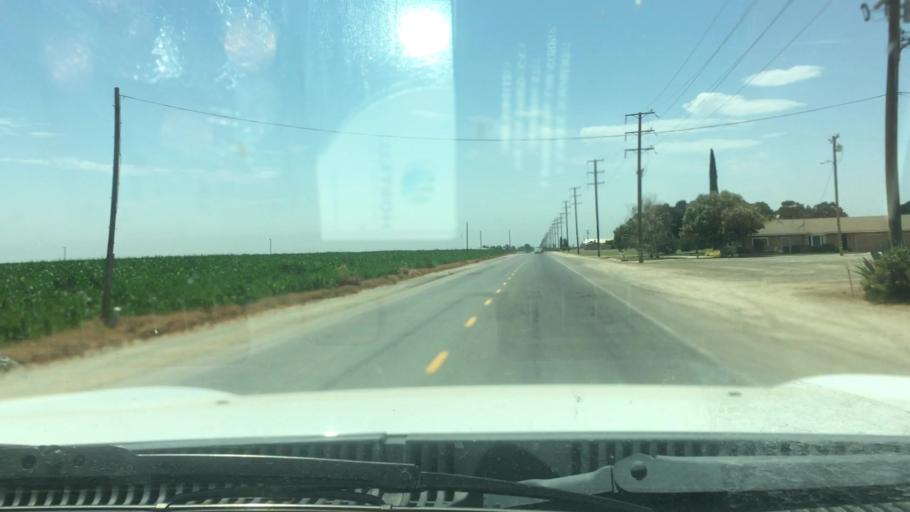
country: US
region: California
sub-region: Tulare County
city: Tipton
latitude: 36.0656
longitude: -119.2632
